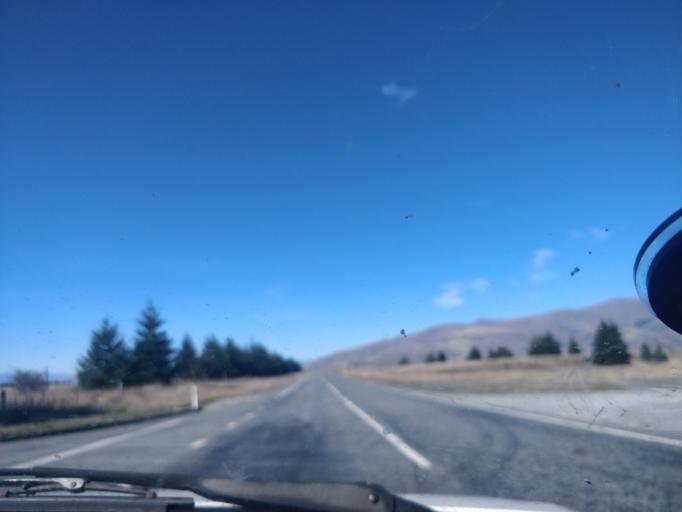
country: NZ
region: Otago
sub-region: Queenstown-Lakes District
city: Wanaka
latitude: -44.2675
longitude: 170.0389
